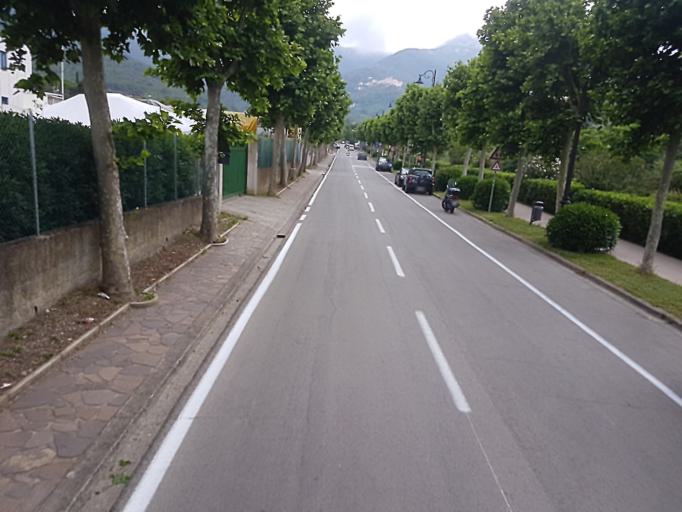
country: IT
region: Tuscany
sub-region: Provincia di Livorno
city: Marciana Marina
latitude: 42.8064
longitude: 10.1929
